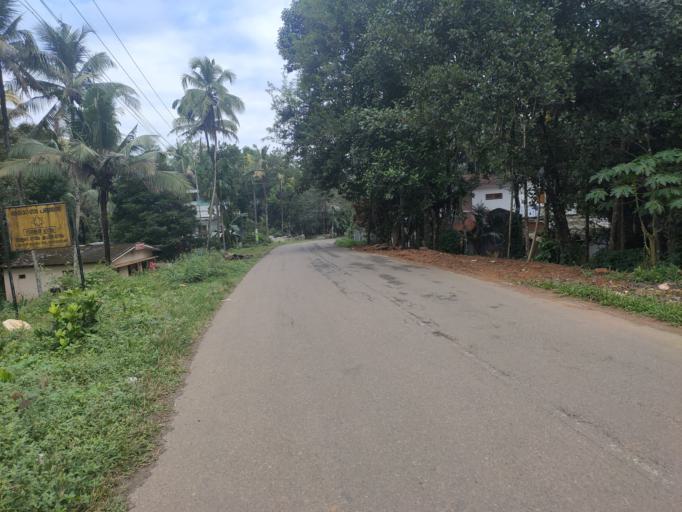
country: IN
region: Kerala
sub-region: Ernakulam
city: Muvattupula
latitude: 9.9903
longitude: 76.6365
